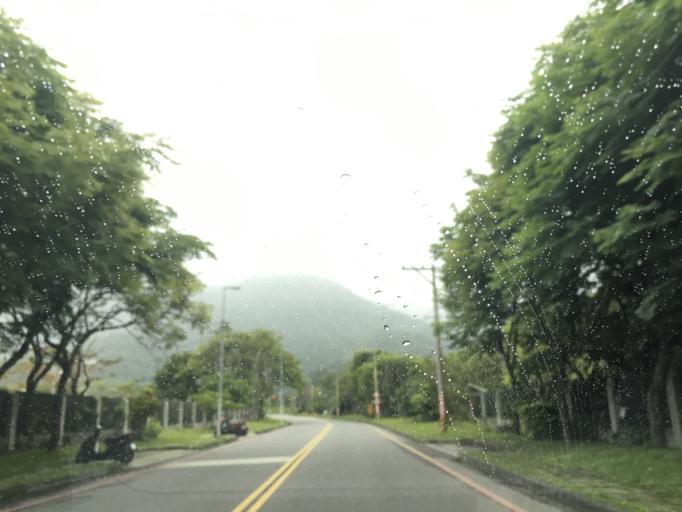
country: TW
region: Taiwan
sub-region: Hualien
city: Hualian
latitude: 23.9998
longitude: 121.5739
